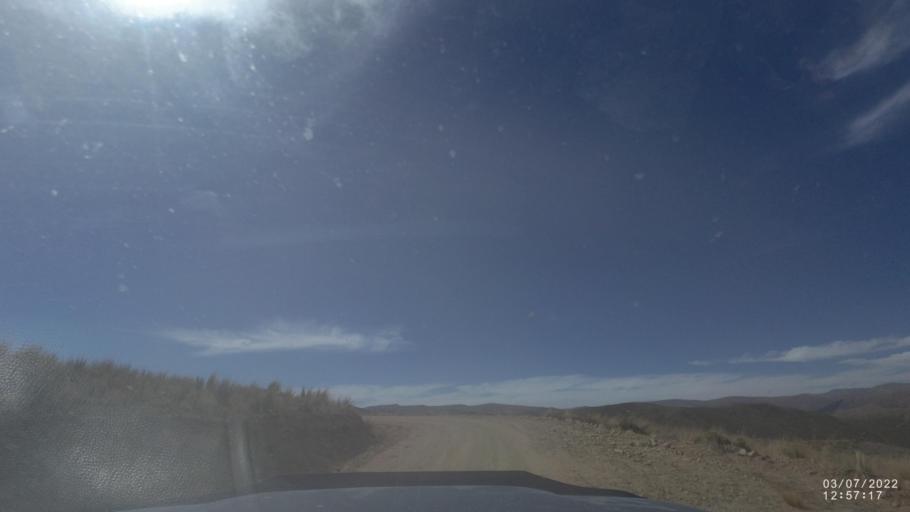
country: BO
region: Cochabamba
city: Sipe Sipe
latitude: -17.7259
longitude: -66.6754
